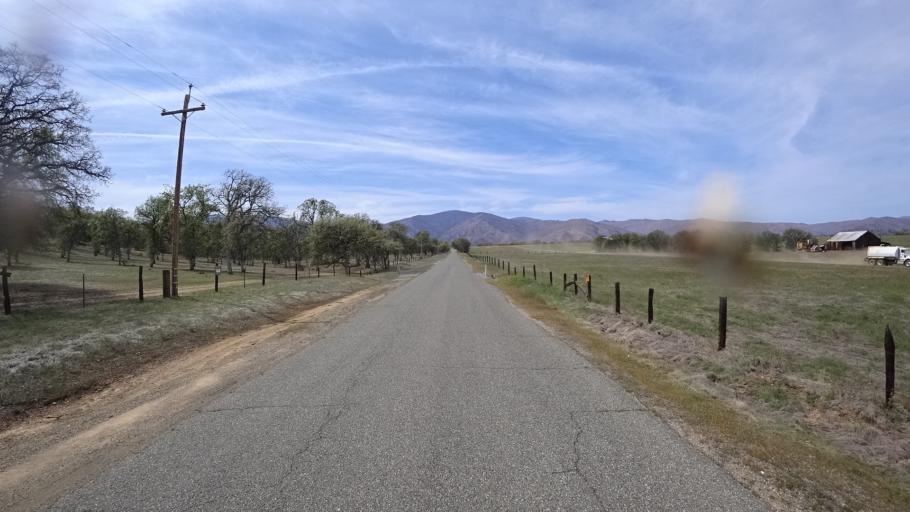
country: US
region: California
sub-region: Glenn County
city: Willows
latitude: 39.5916
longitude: -122.5601
